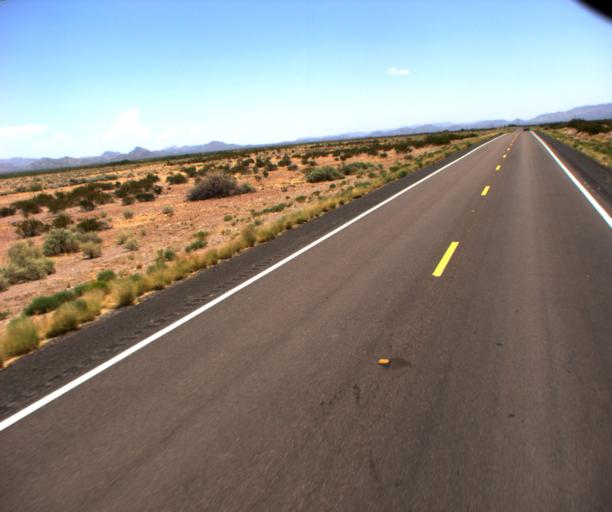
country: US
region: Arizona
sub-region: Graham County
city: Safford
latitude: 32.7892
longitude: -109.5468
